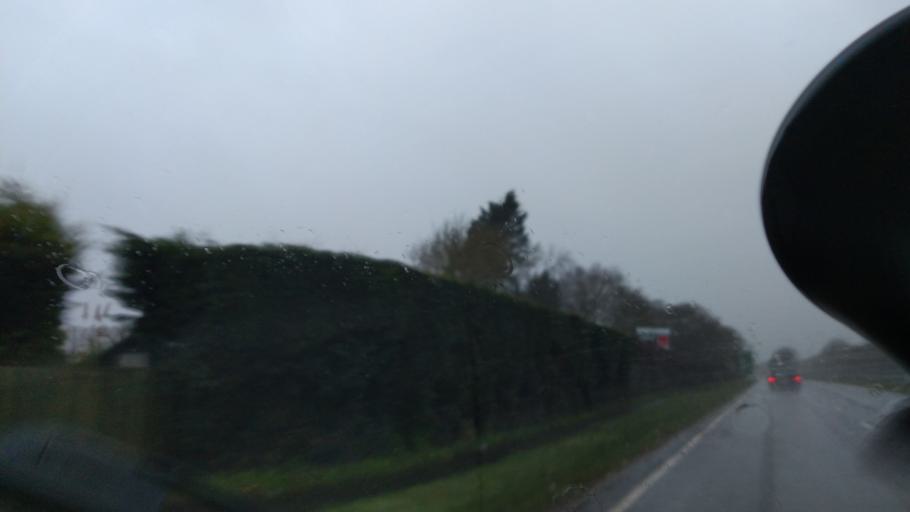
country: GB
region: England
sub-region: West Sussex
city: Rustington
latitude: 50.8416
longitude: -0.5054
